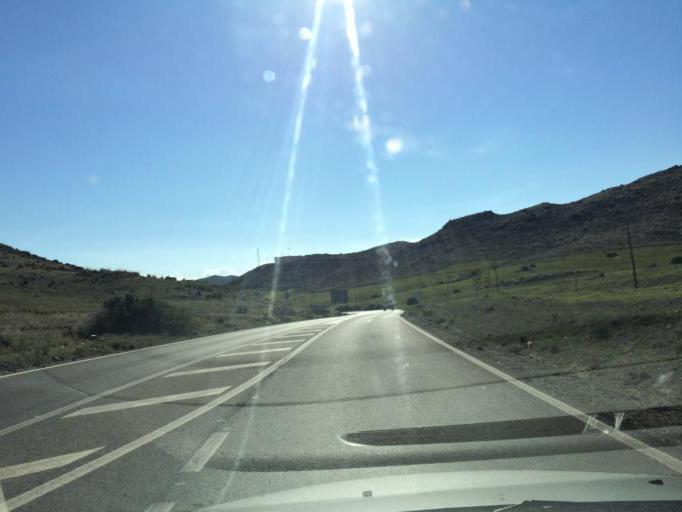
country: ES
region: Andalusia
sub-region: Provincia de Almeria
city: San Jose
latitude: 36.7935
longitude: -2.1133
